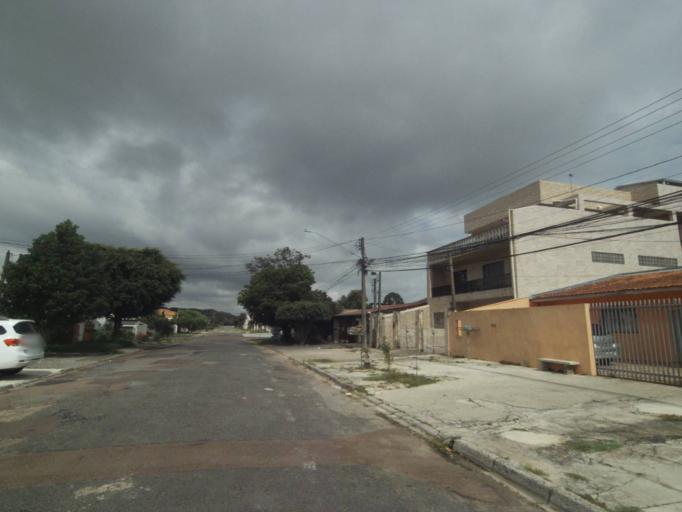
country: BR
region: Parana
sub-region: Pinhais
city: Pinhais
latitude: -25.4527
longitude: -49.2203
